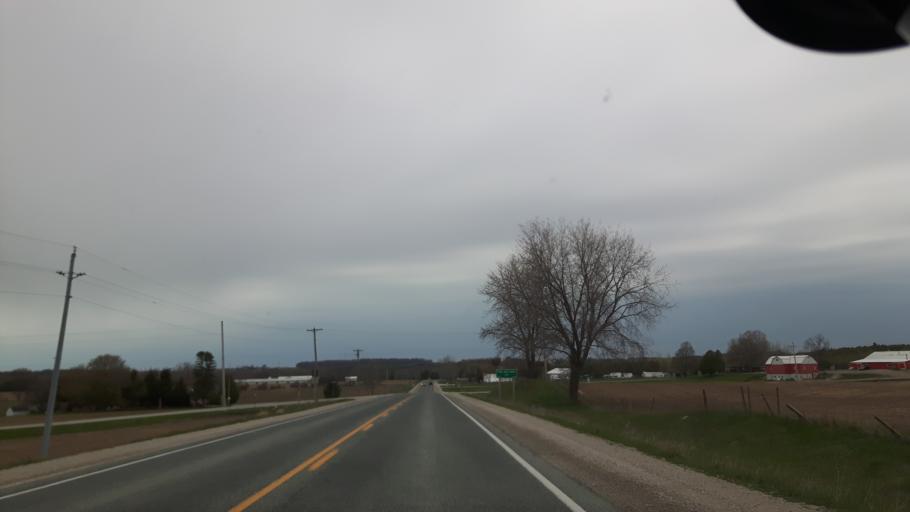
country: CA
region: Ontario
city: Bluewater
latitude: 43.6346
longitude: -81.5801
